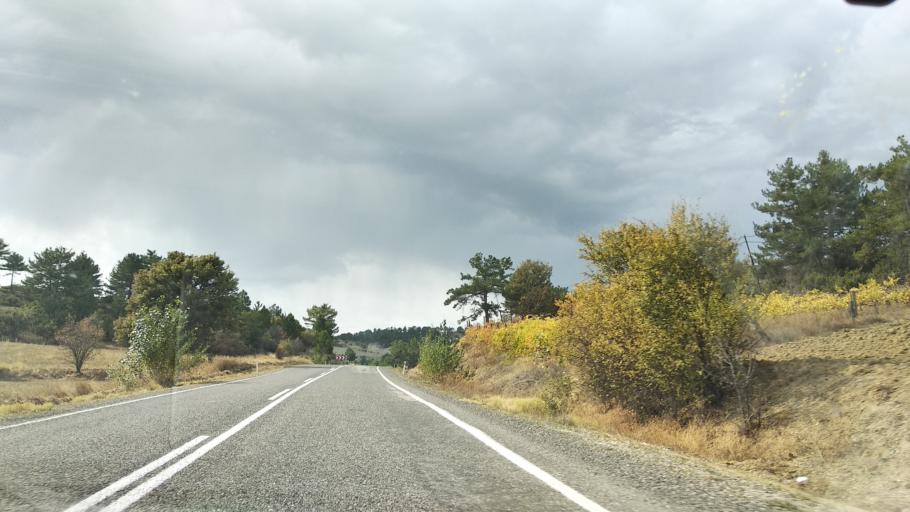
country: TR
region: Bolu
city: Seben
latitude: 40.3598
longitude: 31.4902
